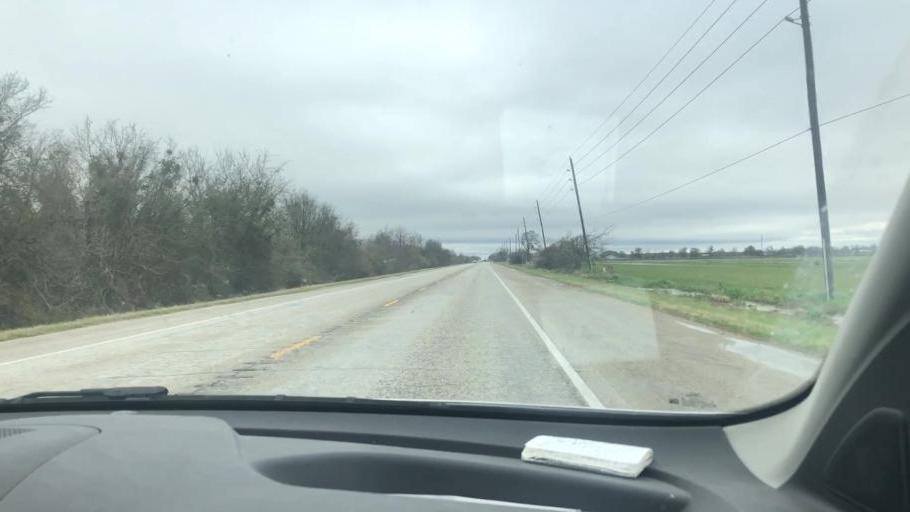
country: US
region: Texas
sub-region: Wharton County
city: Wharton
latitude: 29.2751
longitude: -96.0629
